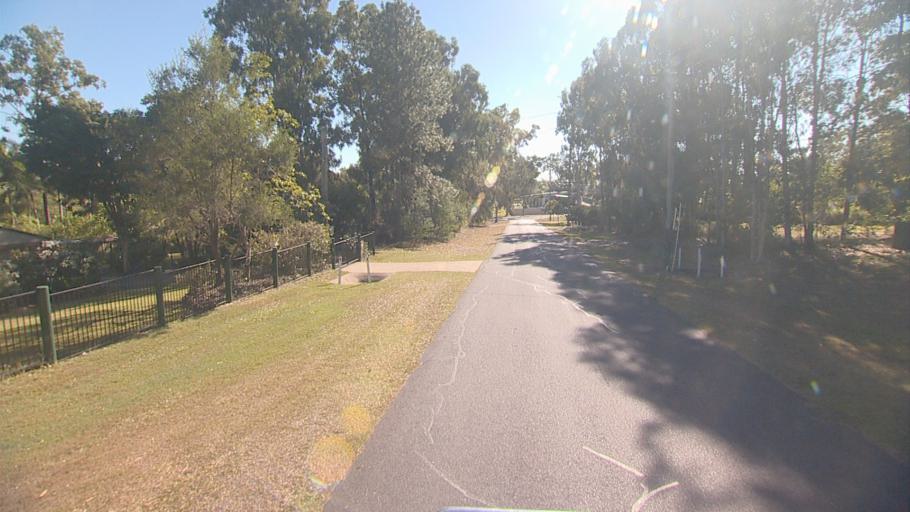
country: AU
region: Queensland
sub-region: Brisbane
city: Forest Lake
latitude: -27.6640
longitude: 153.0112
